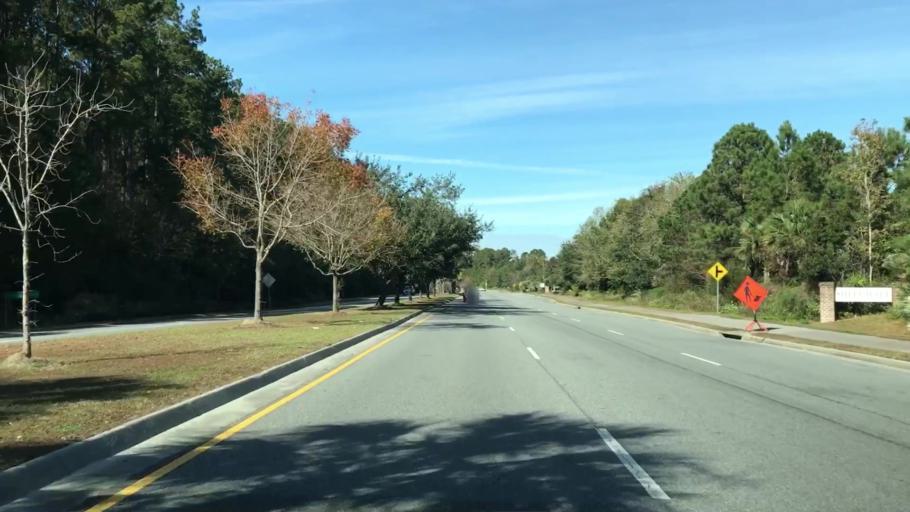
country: US
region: South Carolina
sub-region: Beaufort County
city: Bluffton
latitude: 32.2587
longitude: -80.9037
